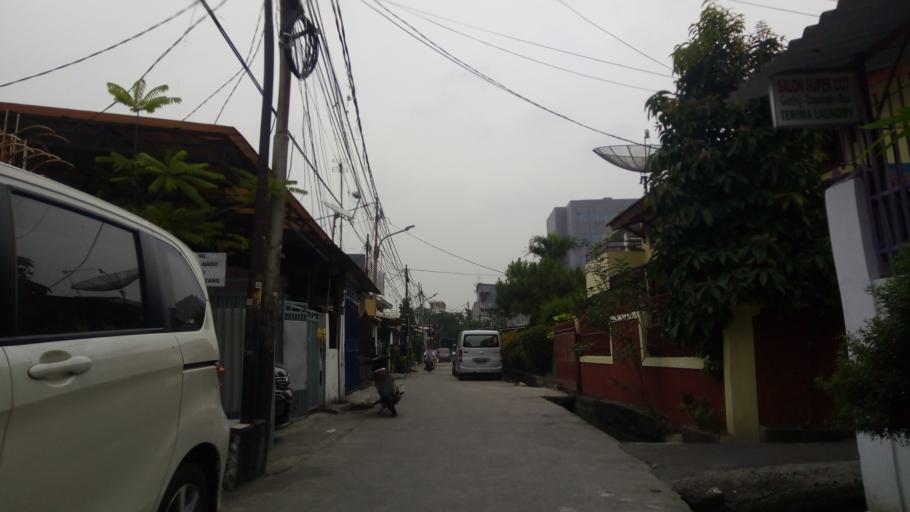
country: ID
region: Jakarta Raya
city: Jakarta
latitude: -6.1524
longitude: 106.8374
